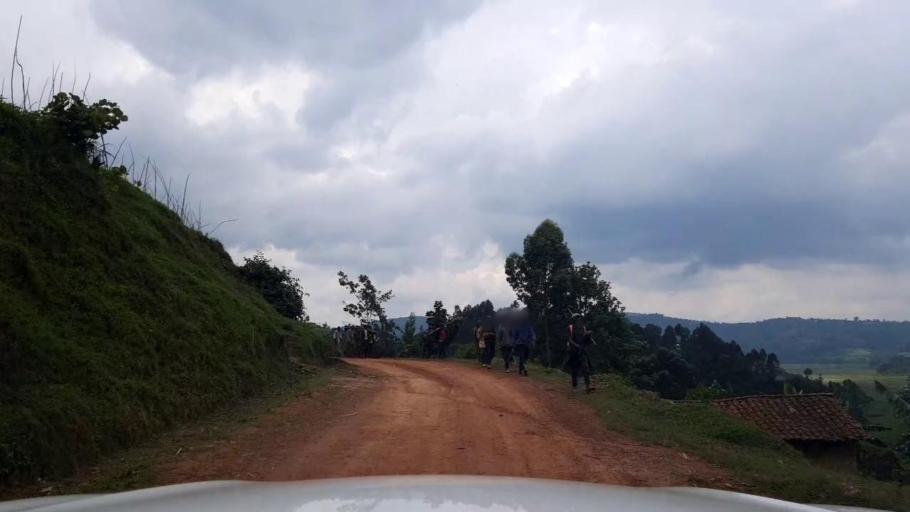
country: UG
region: Western Region
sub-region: Kabale District
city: Kabale
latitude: -1.4273
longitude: 29.8675
